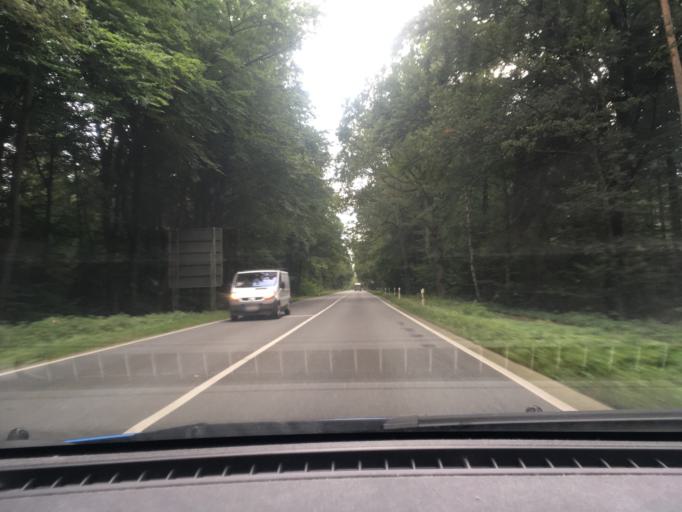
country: DE
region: Lower Saxony
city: Suderburg
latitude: 52.8863
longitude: 10.5053
